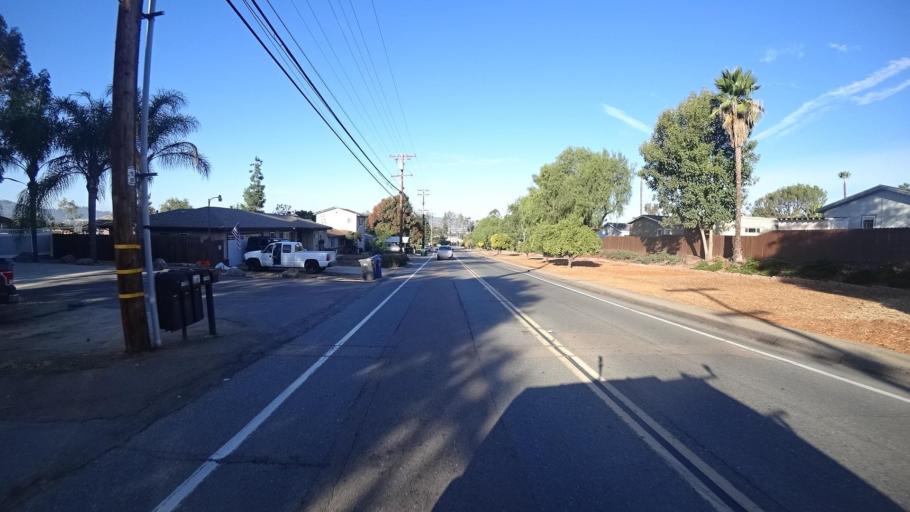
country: US
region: California
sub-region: San Diego County
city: Winter Gardens
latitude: 32.8213
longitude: -116.9424
